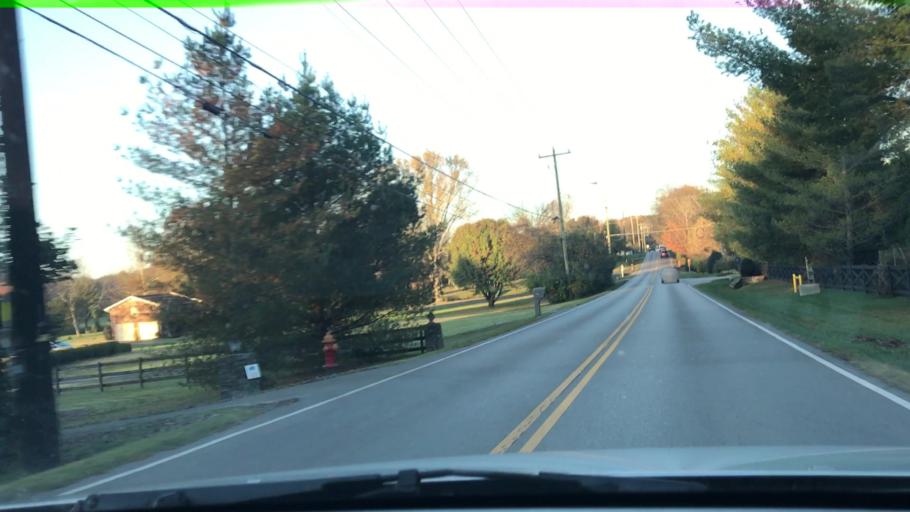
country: US
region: Tennessee
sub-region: Williamson County
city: Brentwood Estates
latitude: 36.0135
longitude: -86.7141
